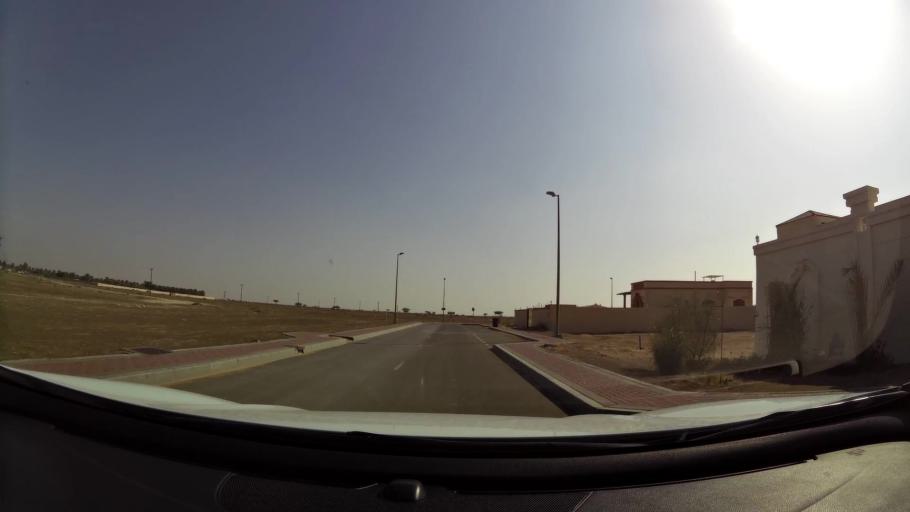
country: AE
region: Abu Dhabi
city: Al Ain
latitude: 24.0859
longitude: 55.9033
